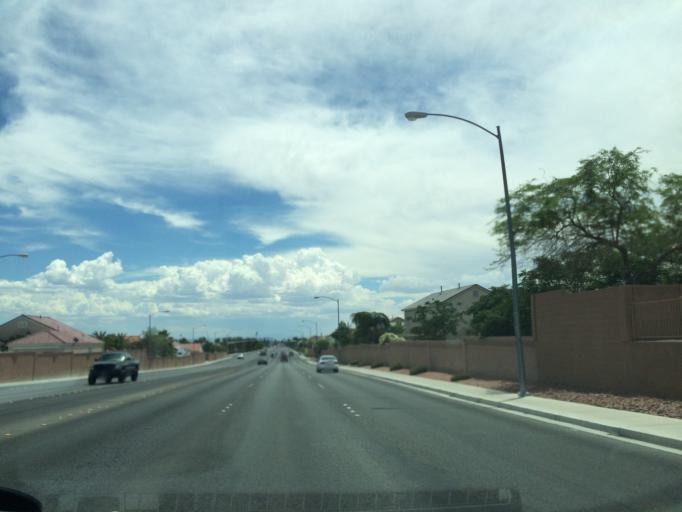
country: US
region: Nevada
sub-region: Clark County
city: North Las Vegas
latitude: 36.2715
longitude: -115.1799
